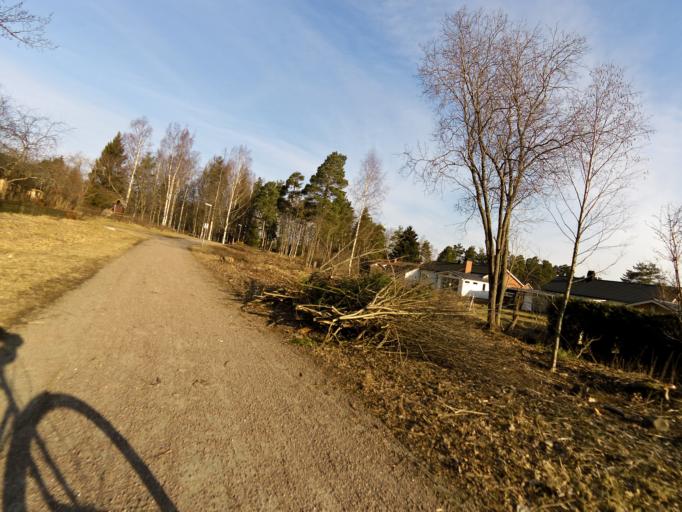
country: SE
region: Gaevleborg
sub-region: Gavle Kommun
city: Gavle
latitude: 60.6572
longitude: 17.1201
